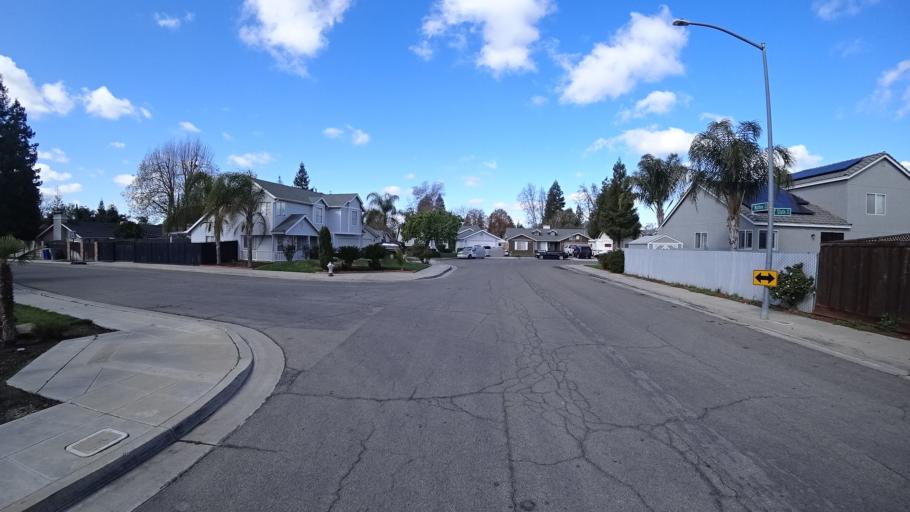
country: US
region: California
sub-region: Fresno County
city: West Park
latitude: 36.8320
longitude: -119.8869
